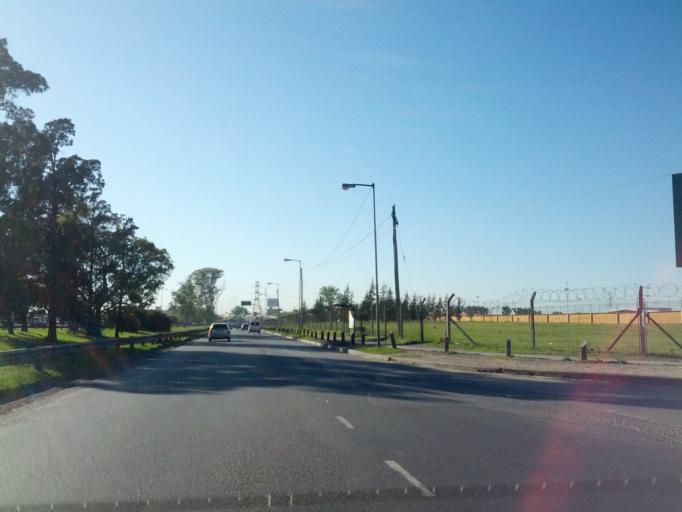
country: AR
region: Buenos Aires F.D.
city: Villa Lugano
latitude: -34.7017
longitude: -58.4664
